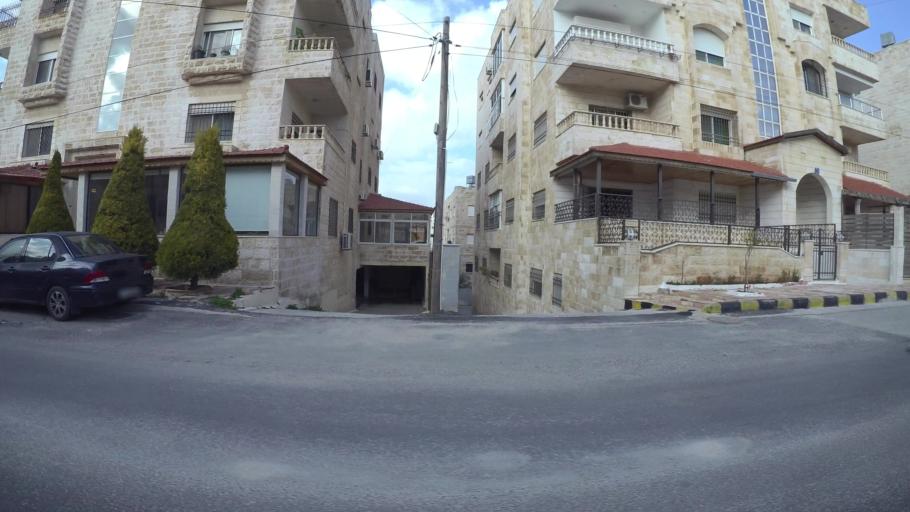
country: JO
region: Amman
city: Al Jubayhah
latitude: 31.9860
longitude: 35.8507
